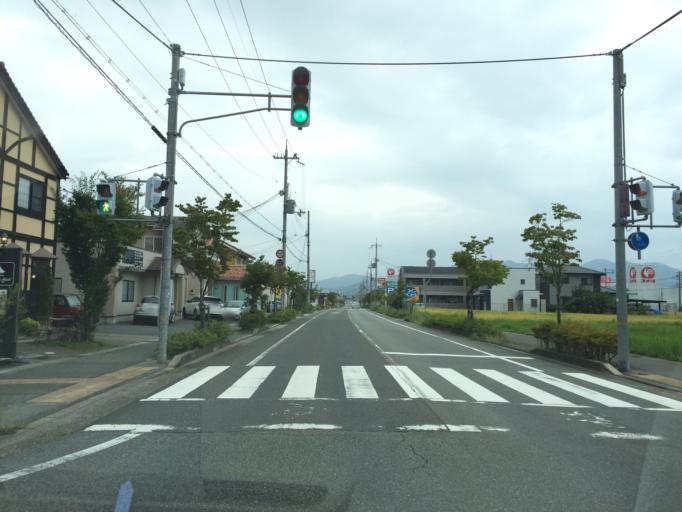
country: JP
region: Hyogo
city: Toyooka
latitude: 35.5372
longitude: 134.8088
